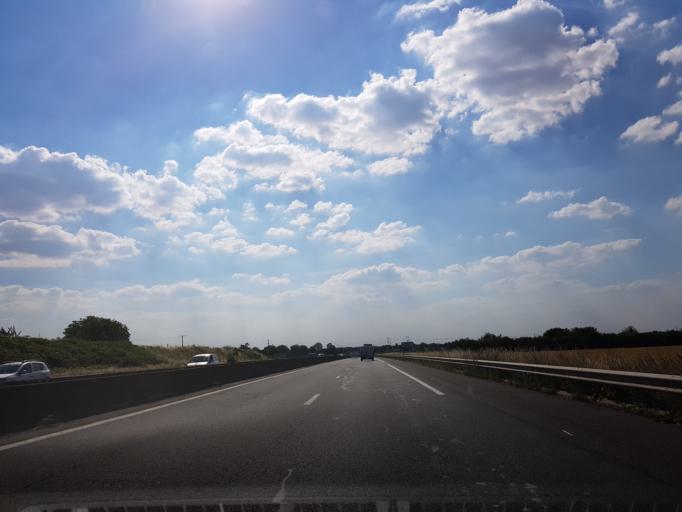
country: FR
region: Nord-Pas-de-Calais
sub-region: Departement du Nord
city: Abscon
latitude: 50.3457
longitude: 3.2936
